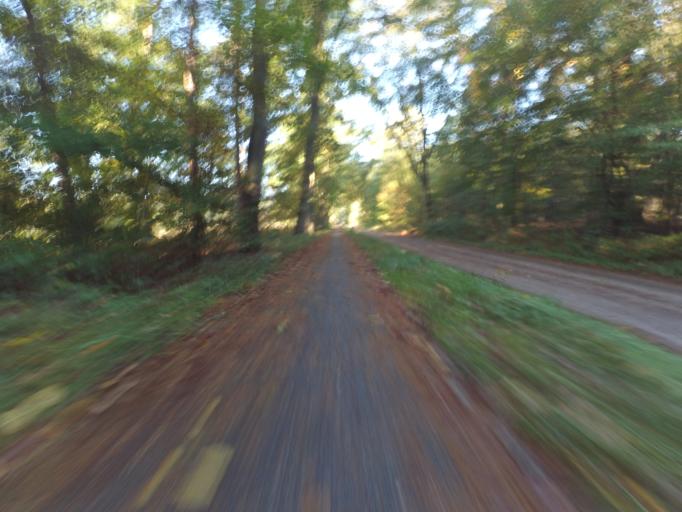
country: NL
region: Gelderland
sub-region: Gemeente Epe
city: Vaassen
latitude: 52.2883
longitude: 5.9101
